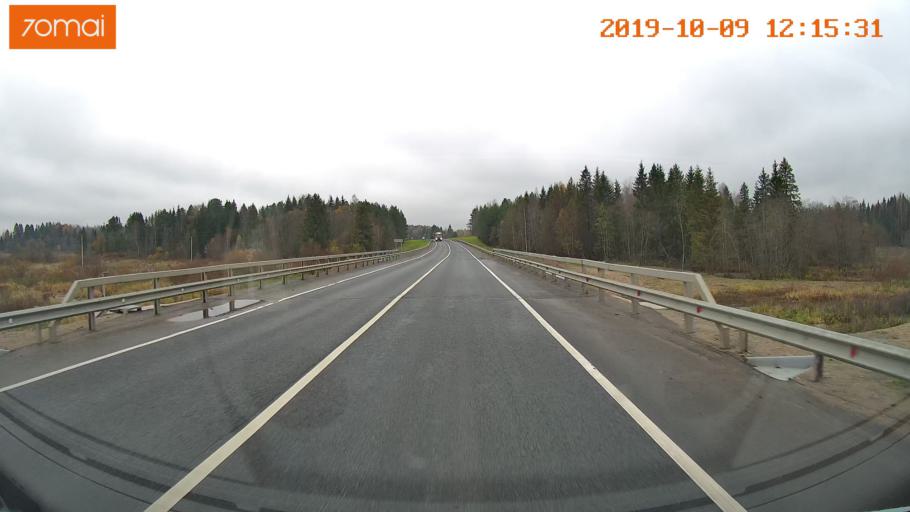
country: RU
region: Jaroslavl
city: Prechistoye
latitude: 58.4824
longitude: 40.3238
